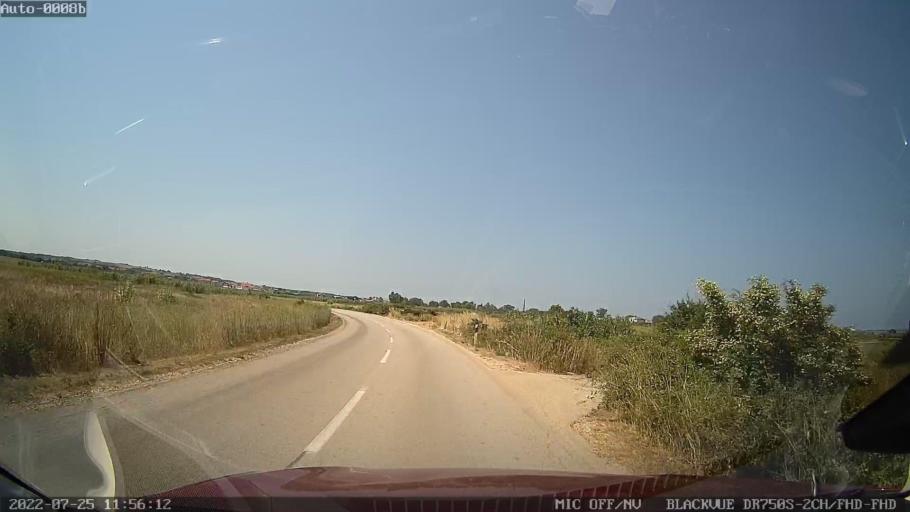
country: HR
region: Zadarska
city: Vrsi
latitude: 44.2517
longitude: 15.2194
